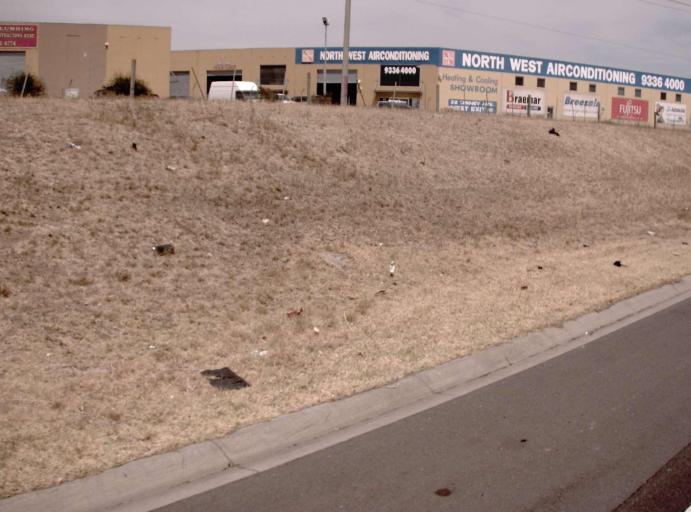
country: AU
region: Victoria
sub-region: Moonee Valley
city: Keilor East
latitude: -37.7328
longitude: 144.8541
